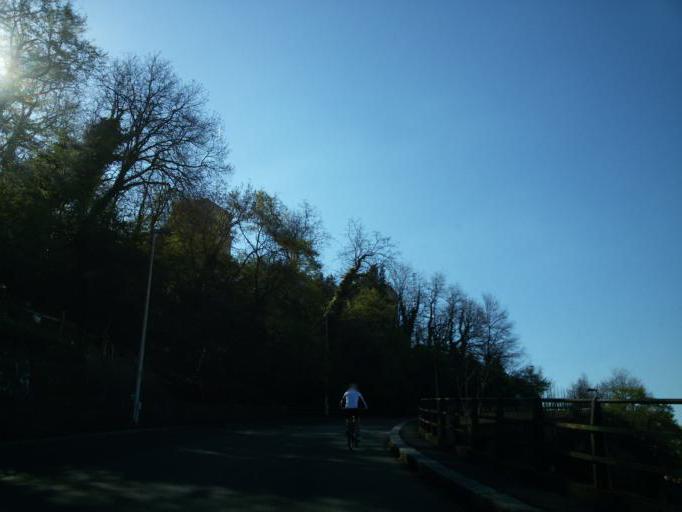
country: IT
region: Liguria
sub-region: Provincia di Genova
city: Genoa
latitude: 44.4261
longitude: 8.9097
